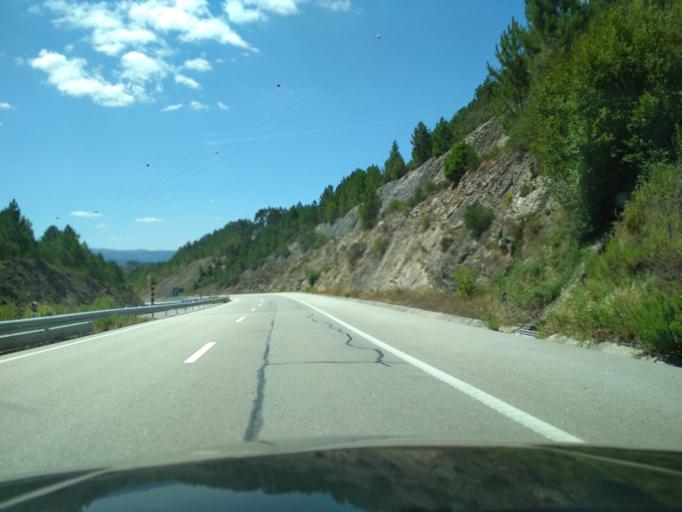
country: PT
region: Vila Real
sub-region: Ribeira de Pena
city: Ribeira de Pena
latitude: 41.4774
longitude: -7.8795
